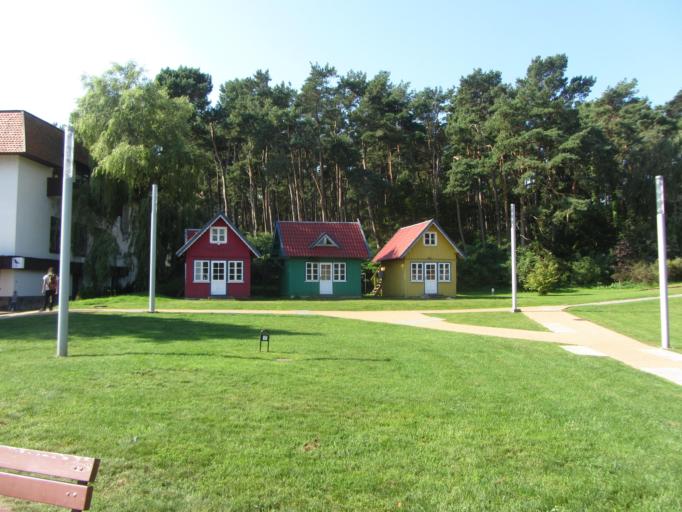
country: LT
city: Nida
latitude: 55.3058
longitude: 21.0069
